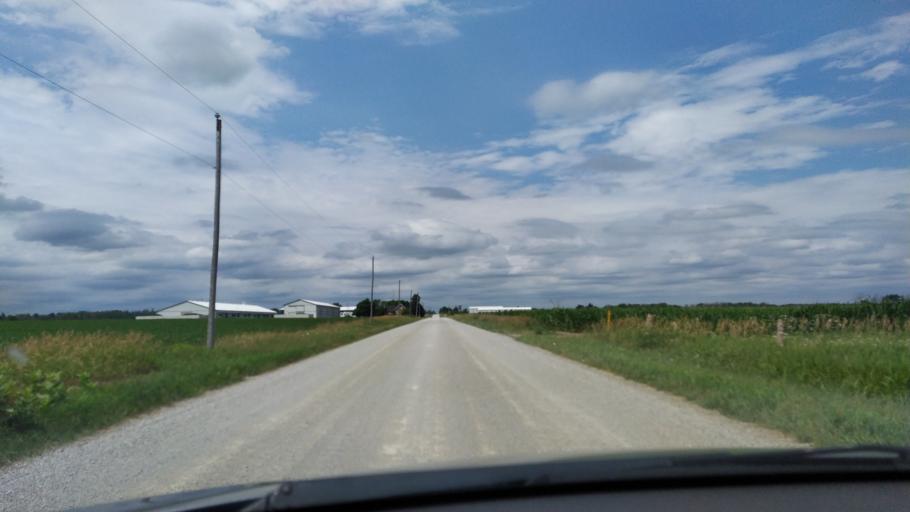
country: CA
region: Ontario
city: Stratford
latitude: 43.3564
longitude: -80.9126
